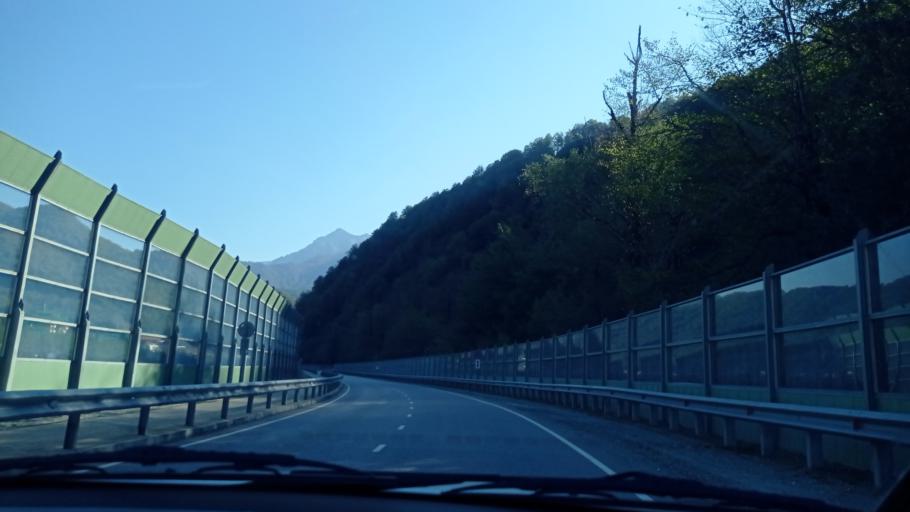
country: RU
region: Krasnodarskiy
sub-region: Sochi City
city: Krasnaya Polyana
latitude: 43.6941
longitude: 40.2692
